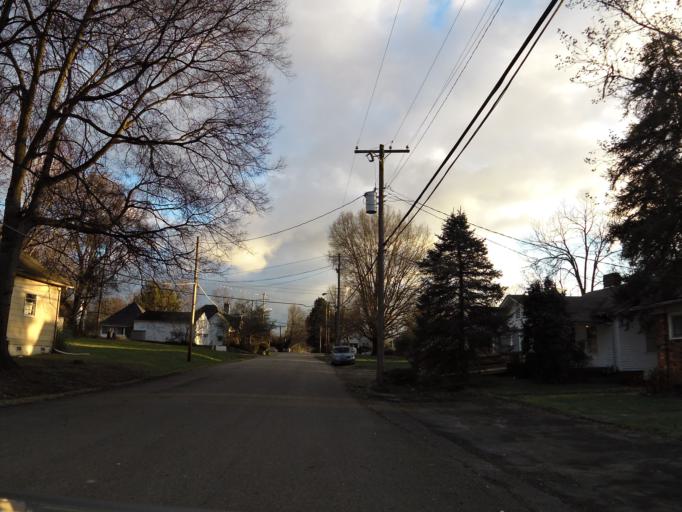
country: US
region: Tennessee
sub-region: Knox County
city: Knoxville
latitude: 35.9997
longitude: -83.9323
